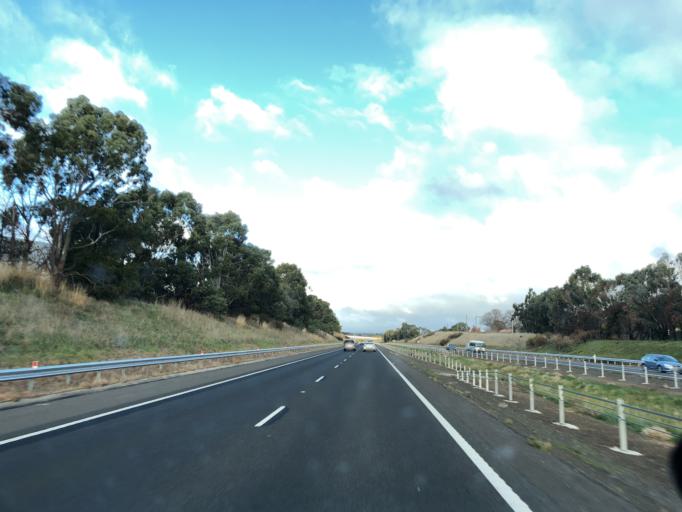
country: AU
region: Victoria
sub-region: Mount Alexander
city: Castlemaine
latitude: -37.2346
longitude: 144.4508
